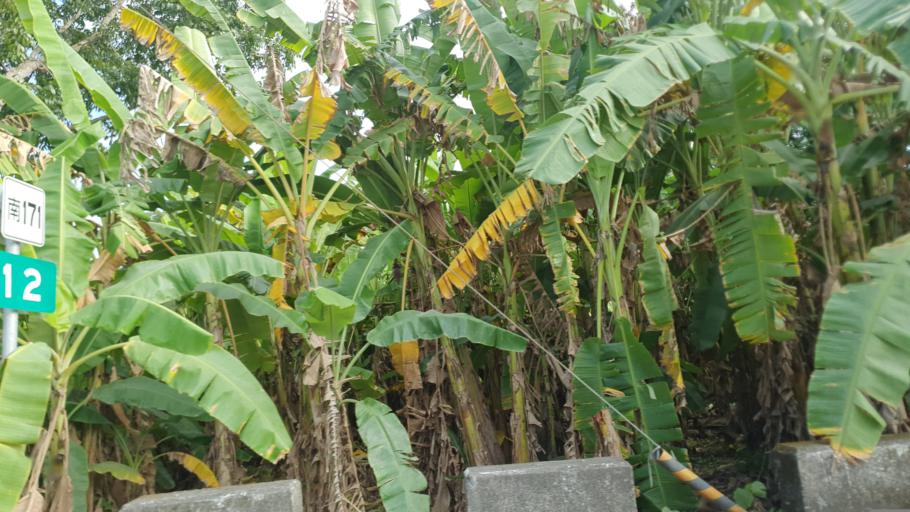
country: TW
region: Taiwan
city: Yujing
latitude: 23.0363
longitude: 120.4176
